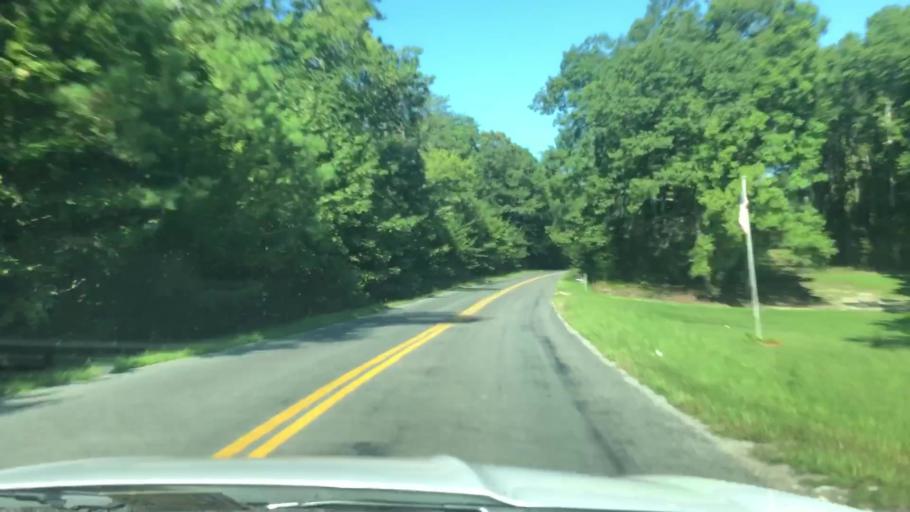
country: US
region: Virginia
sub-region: New Kent County
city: New Kent
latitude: 37.4835
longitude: -76.9258
